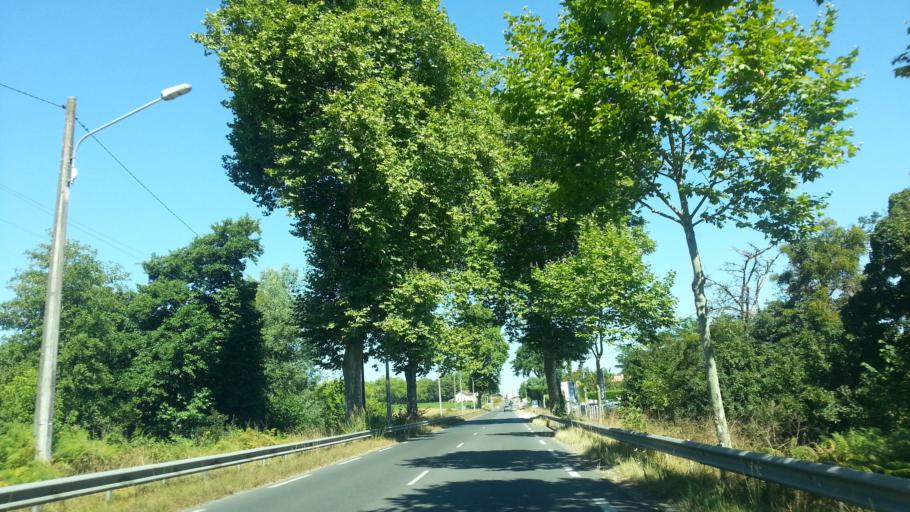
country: FR
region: Aquitaine
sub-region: Departement de la Gironde
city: Cadaujac
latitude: 44.7423
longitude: -0.5411
